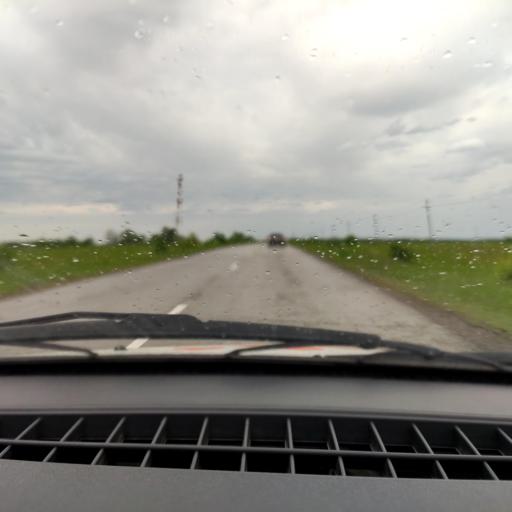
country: RU
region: Bashkortostan
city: Kudeyevskiy
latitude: 54.8395
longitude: 56.7945
